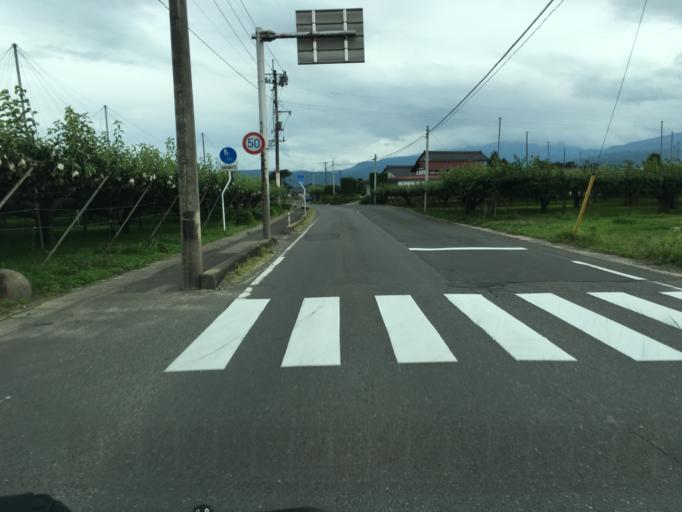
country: JP
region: Fukushima
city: Fukushima-shi
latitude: 37.7768
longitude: 140.4063
